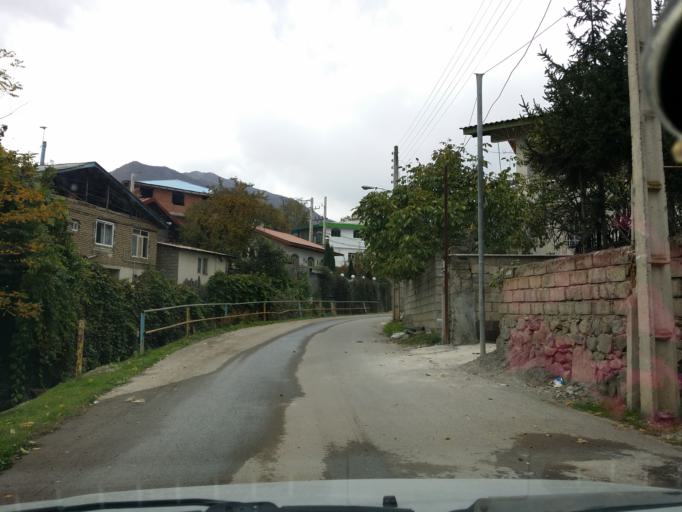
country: IR
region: Mazandaran
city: `Abbasabad
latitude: 36.5002
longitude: 51.1460
